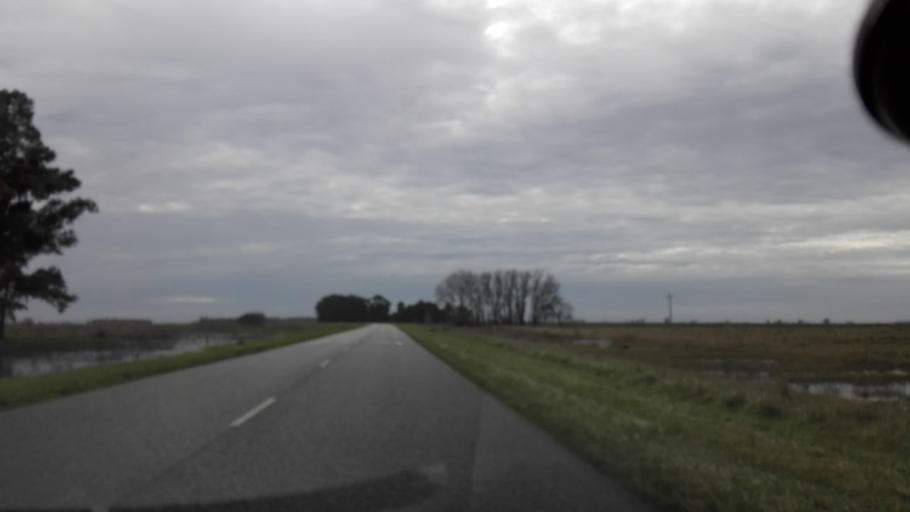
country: AR
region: Buenos Aires
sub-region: Partido de Rauch
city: Rauch
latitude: -36.4589
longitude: -59.0165
